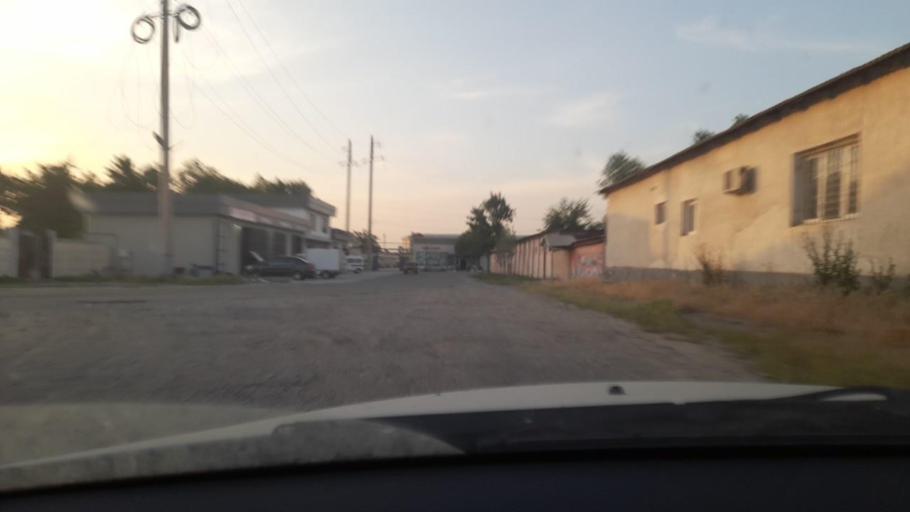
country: UZ
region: Sirdaryo
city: Guliston
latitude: 40.5109
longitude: 68.7621
